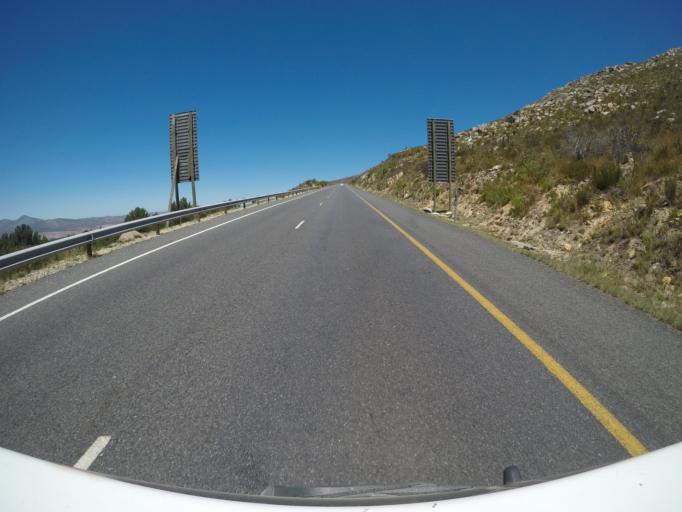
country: ZA
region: Western Cape
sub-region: Overberg District Municipality
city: Grabouw
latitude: -34.2190
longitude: 19.1857
